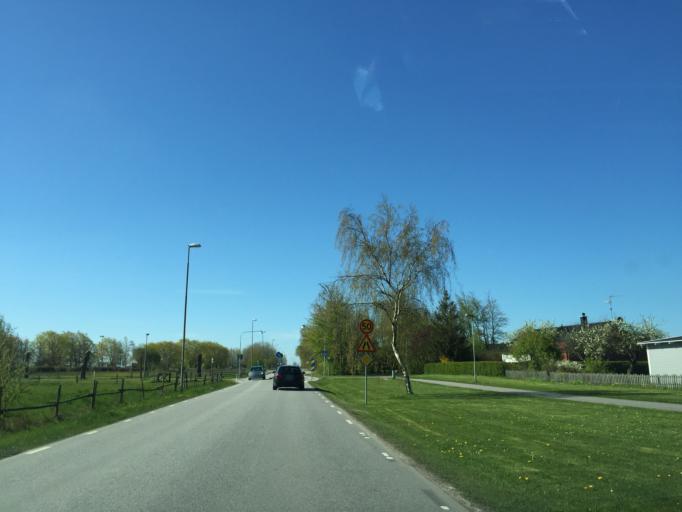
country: SE
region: Skane
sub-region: Staffanstorps Kommun
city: Staffanstorp
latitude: 55.6375
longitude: 13.2145
